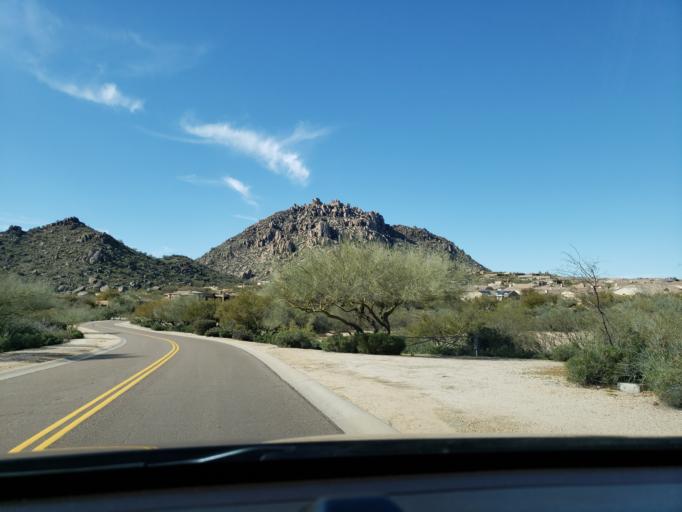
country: US
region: Arizona
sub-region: Maricopa County
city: Carefree
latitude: 33.7058
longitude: -111.8307
